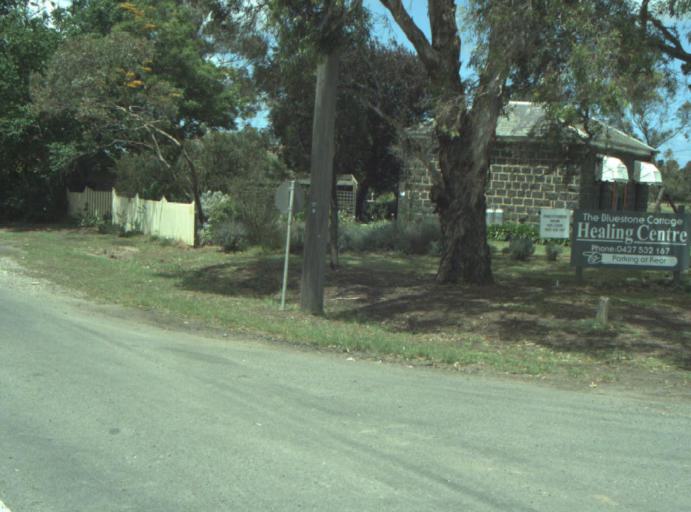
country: AU
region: Victoria
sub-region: Greater Geelong
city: Breakwater
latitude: -38.1979
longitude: 144.3626
